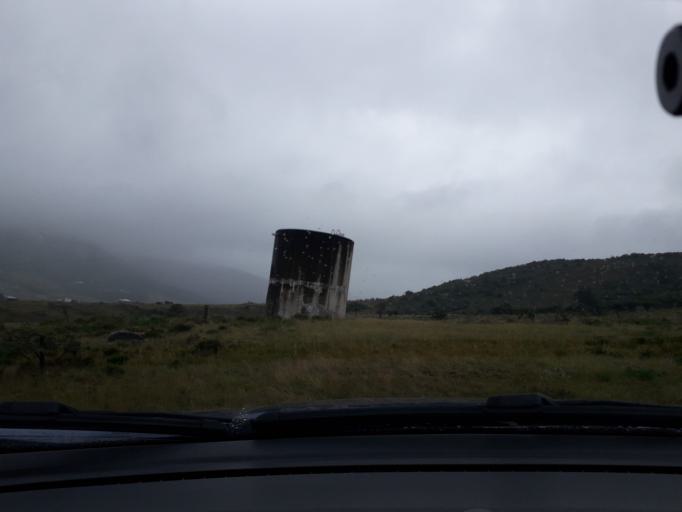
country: ZA
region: Eastern Cape
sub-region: Buffalo City Metropolitan Municipality
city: Bhisho
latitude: -32.7297
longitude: 27.3712
